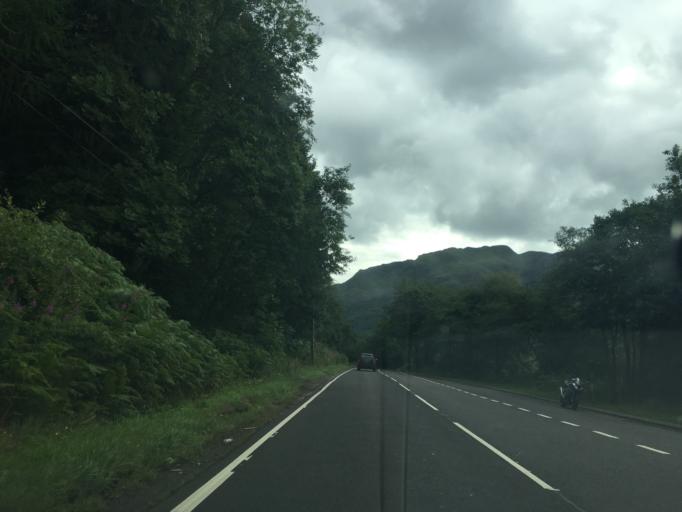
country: GB
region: Scotland
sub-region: Stirling
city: Callander
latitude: 56.3078
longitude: -4.3232
